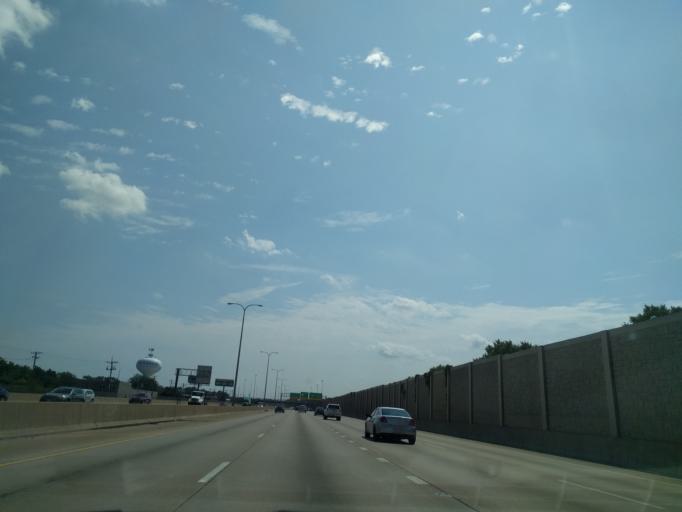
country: US
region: Illinois
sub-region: Cook County
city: South Holland
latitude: 41.5918
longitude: -87.5836
